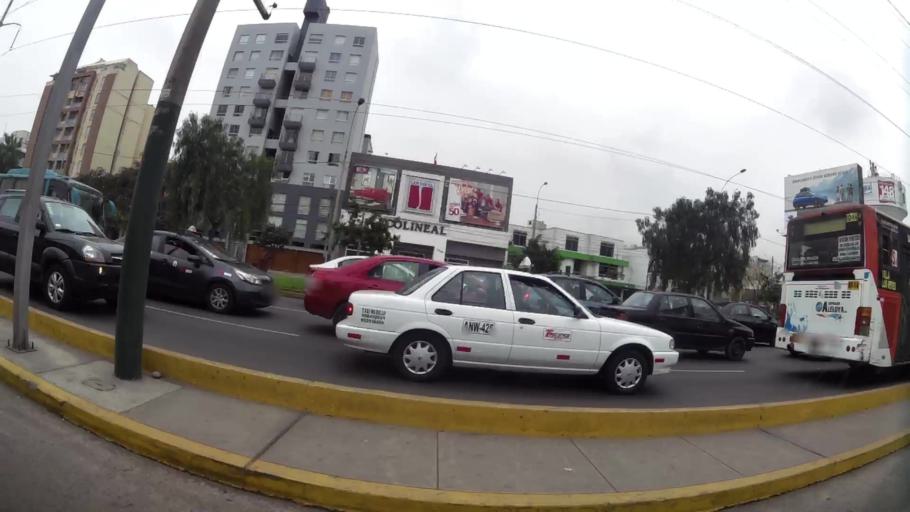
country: PE
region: Lima
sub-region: Lima
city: San Luis
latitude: -12.1106
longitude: -76.9813
